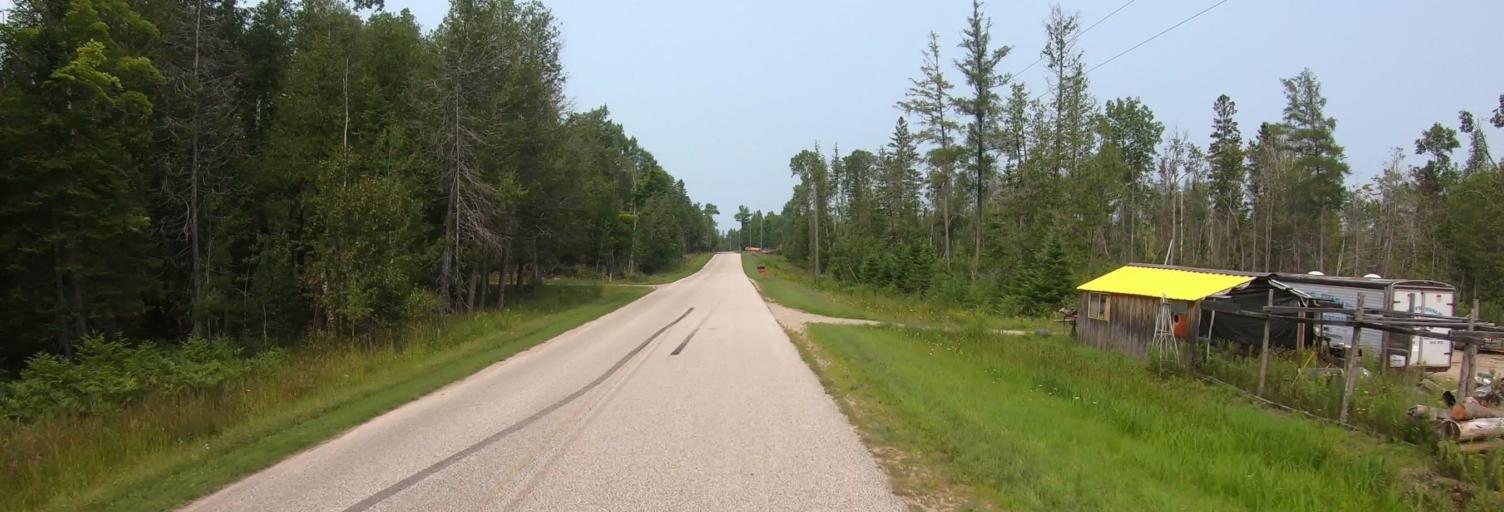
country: CA
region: Ontario
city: Thessalon
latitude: 45.9883
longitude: -83.7391
